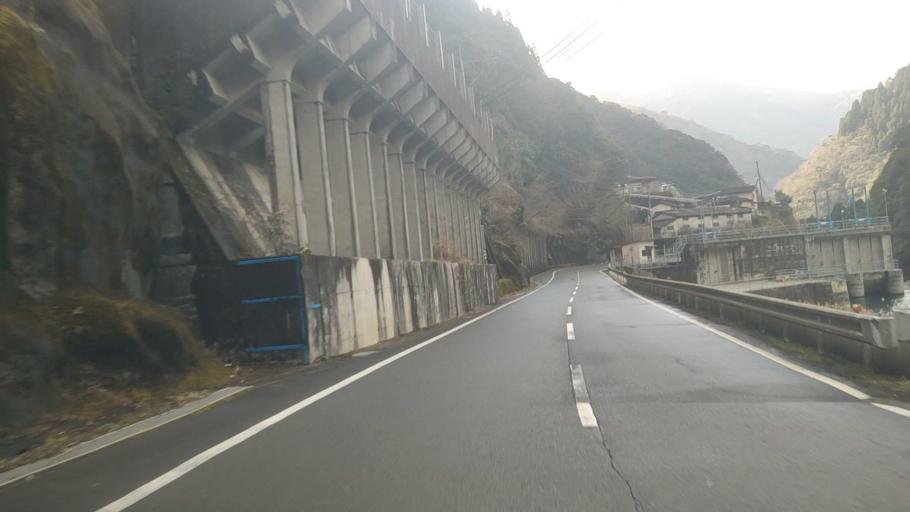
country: JP
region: Kumamoto
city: Hitoyoshi
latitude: 32.4285
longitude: 130.8584
